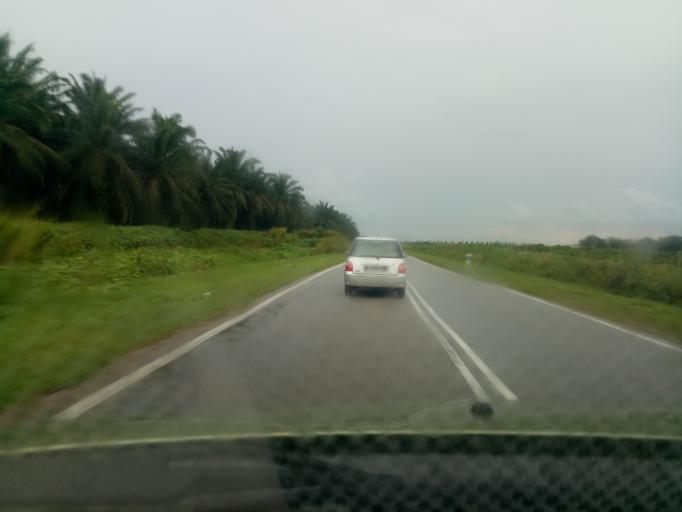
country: MY
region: Kedah
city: Sungai Petani
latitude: 5.5733
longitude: 100.5779
